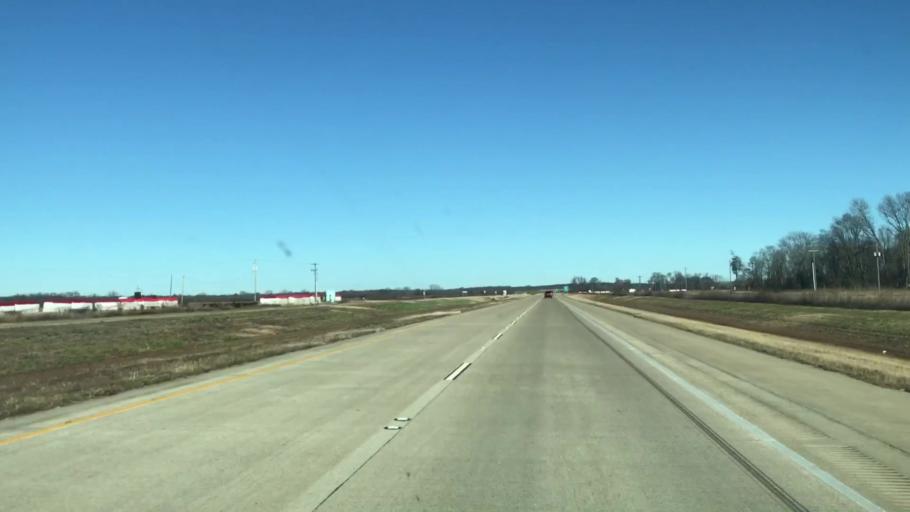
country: US
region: Louisiana
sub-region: Caddo Parish
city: Oil City
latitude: 32.7503
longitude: -93.8815
